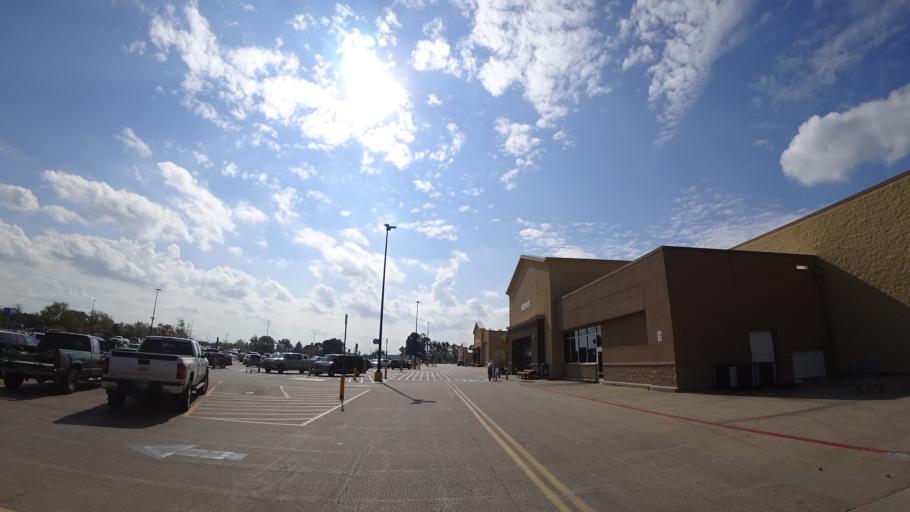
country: US
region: Michigan
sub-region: Saint Joseph County
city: Three Rivers
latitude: 41.9425
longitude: -85.6558
